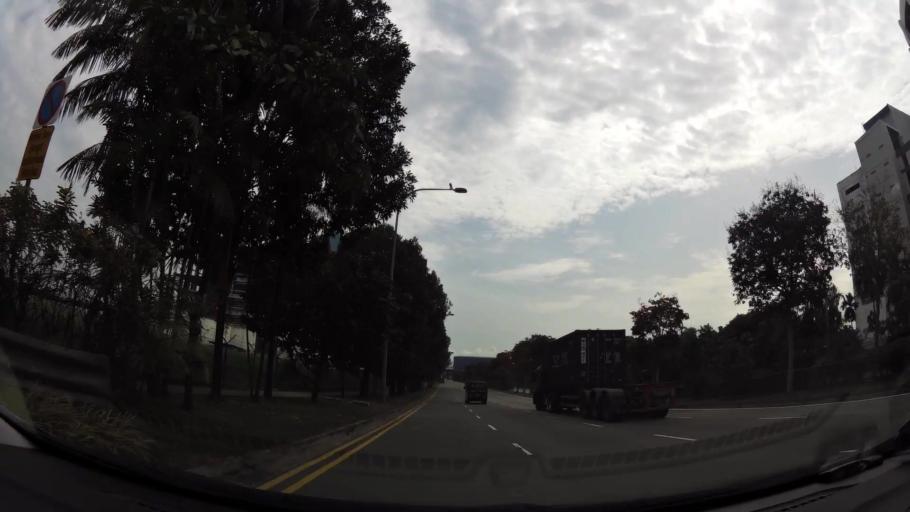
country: SG
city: Singapore
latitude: 1.3144
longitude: 103.7130
